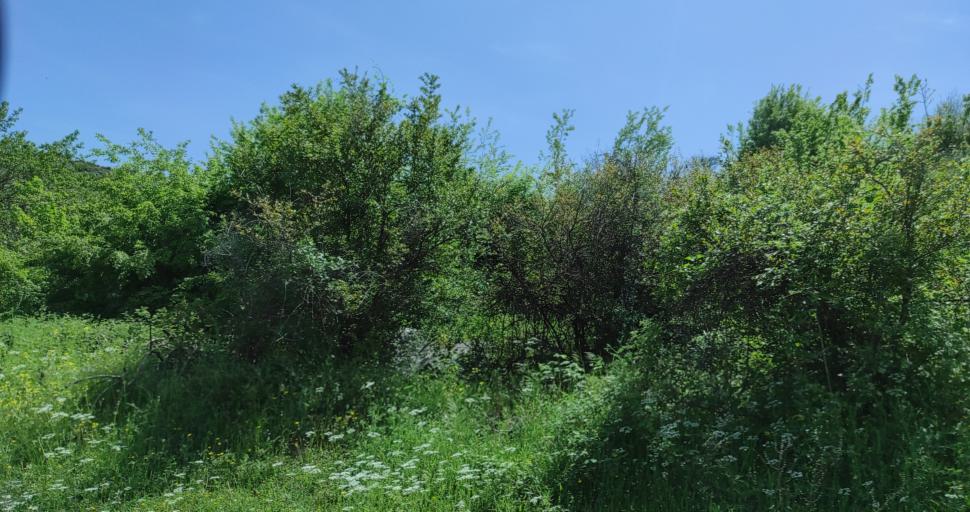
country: AL
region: Shkoder
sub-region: Rrethi i Shkodres
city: Guri i Zi
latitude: 42.1173
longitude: 19.5799
